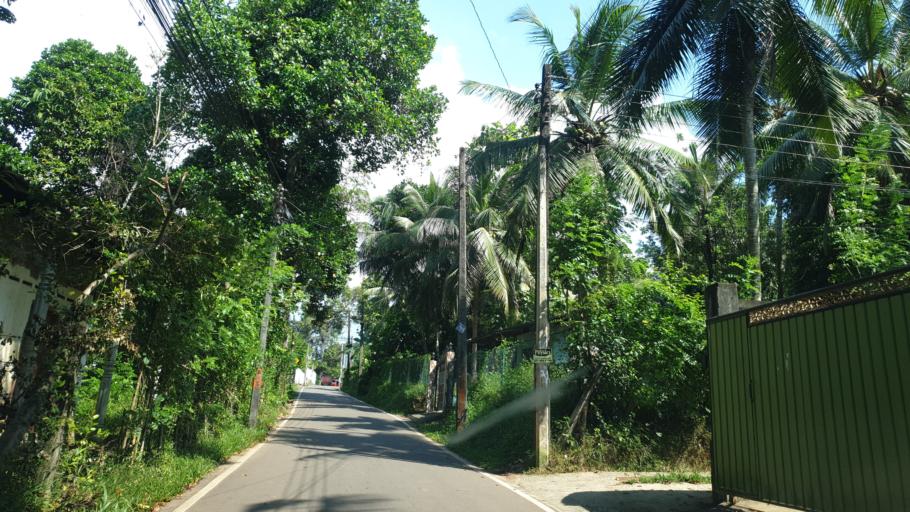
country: LK
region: Western
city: Panadura
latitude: 6.7128
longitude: 79.9604
